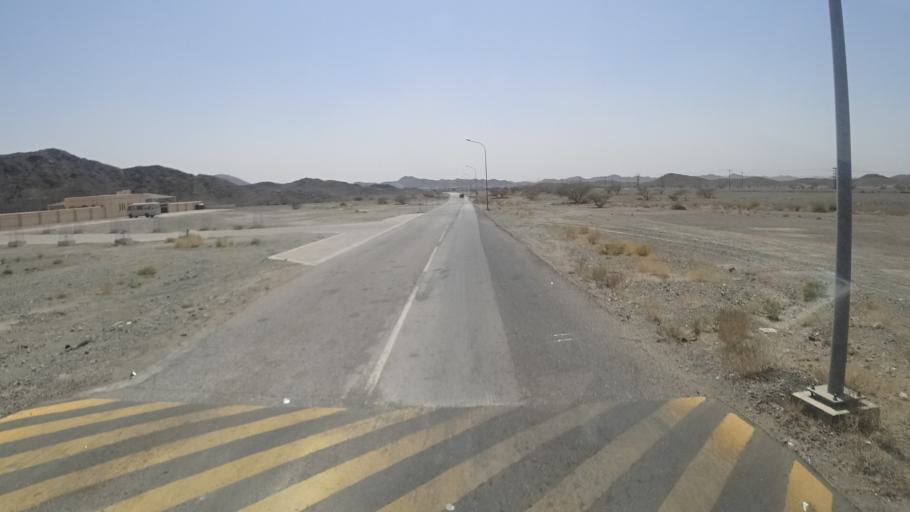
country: OM
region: Ash Sharqiyah
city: Ibra'
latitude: 22.6637
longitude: 58.5283
